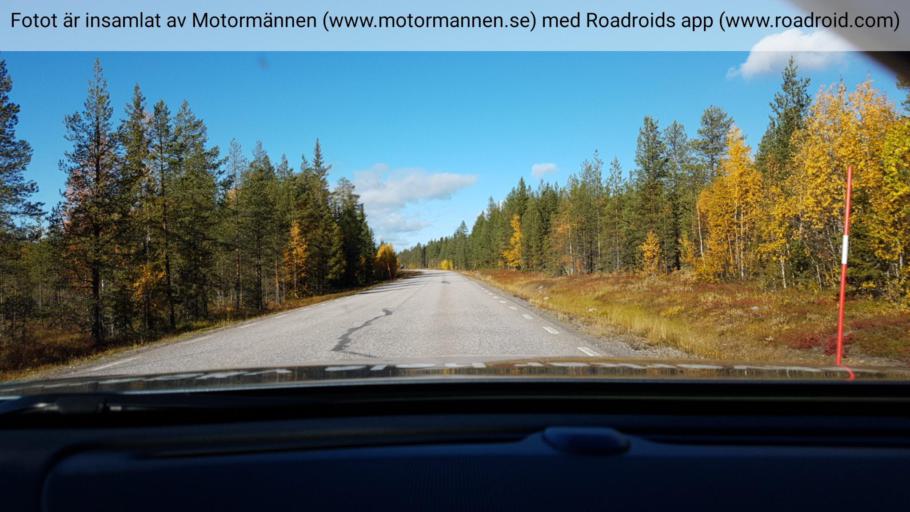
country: SE
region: Norrbotten
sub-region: Arvidsjaurs Kommun
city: Arvidsjaur
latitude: 65.6784
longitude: 18.8260
